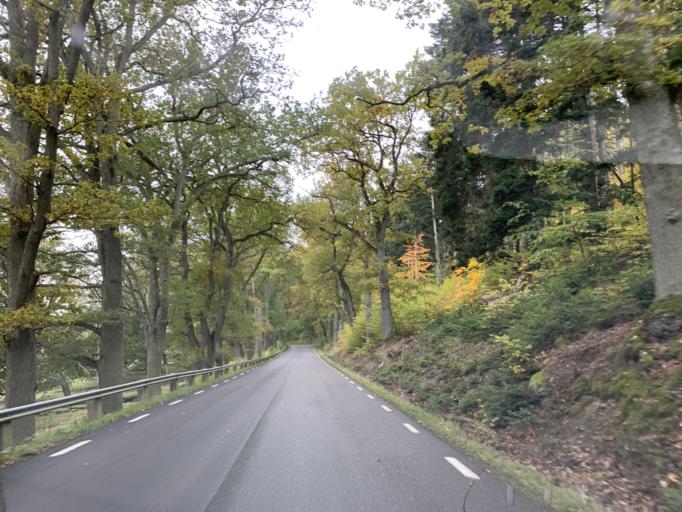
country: SE
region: Stockholm
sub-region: Nynashamns Kommun
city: Osmo
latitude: 58.9643
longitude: 17.7694
